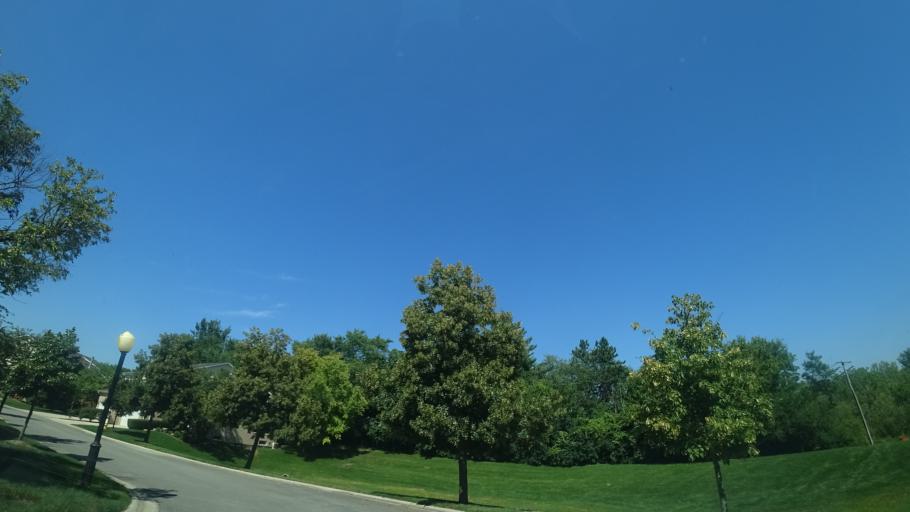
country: US
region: Illinois
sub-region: Will County
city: Mokena
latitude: 41.5664
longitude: -87.9026
